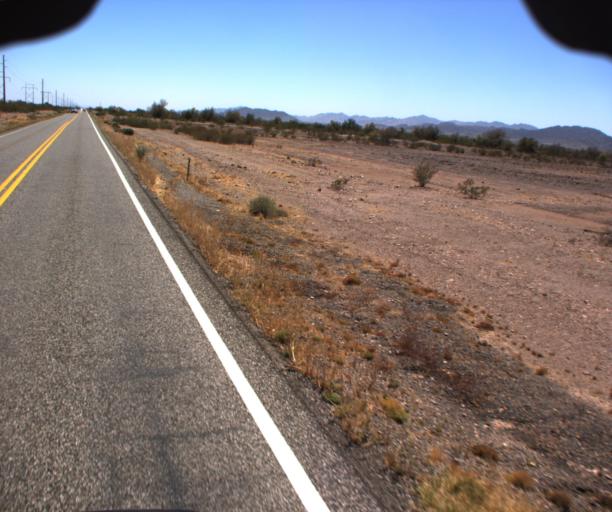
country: US
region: Arizona
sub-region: La Paz County
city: Quartzsite
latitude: 33.7584
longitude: -114.2170
